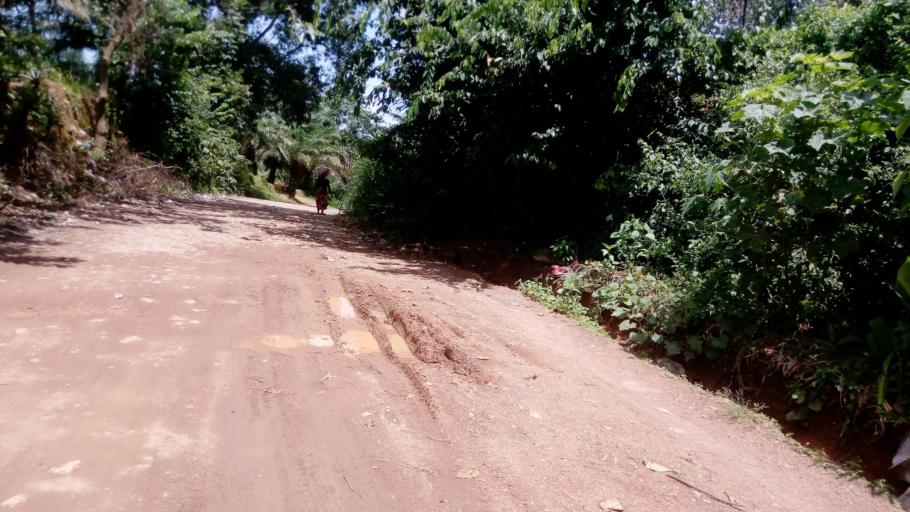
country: SL
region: Northern Province
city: Binkolo
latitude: 8.9537
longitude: -11.9760
